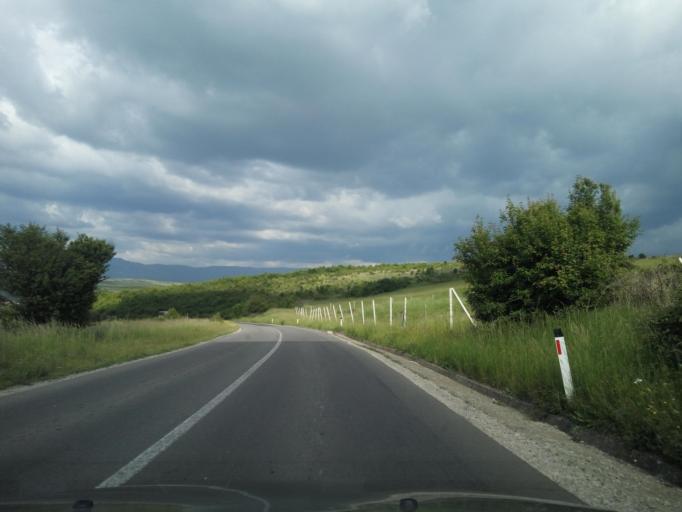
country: XK
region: Gjakova
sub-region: Komuna e Gjakoves
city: Gjakove
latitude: 42.4313
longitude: 20.4534
